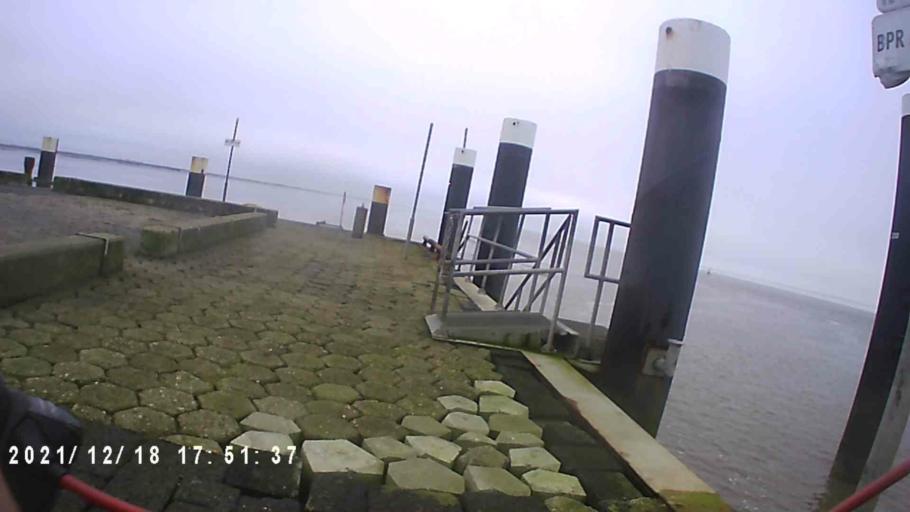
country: NL
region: Friesland
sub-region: Gemeente Dongeradeel
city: Holwerd
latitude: 53.3956
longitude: 5.8782
